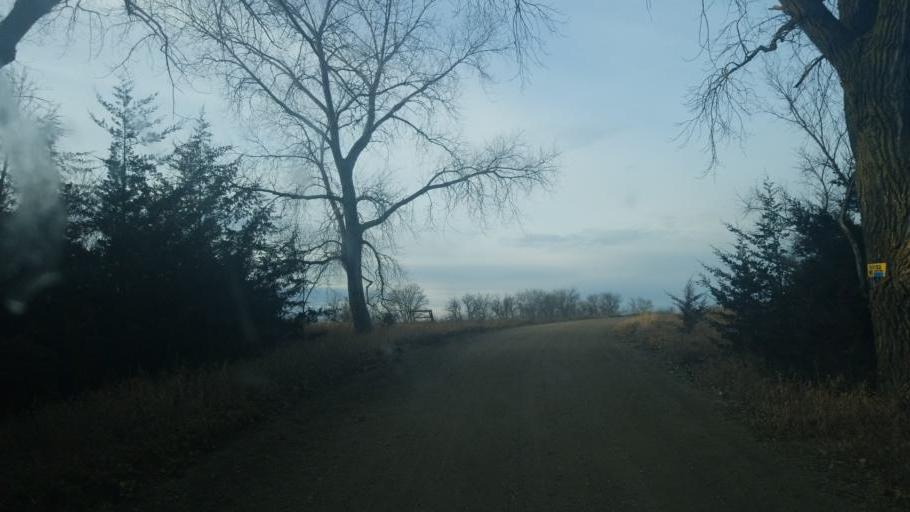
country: US
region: Nebraska
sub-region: Knox County
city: Center
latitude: 42.6813
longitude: -97.8181
